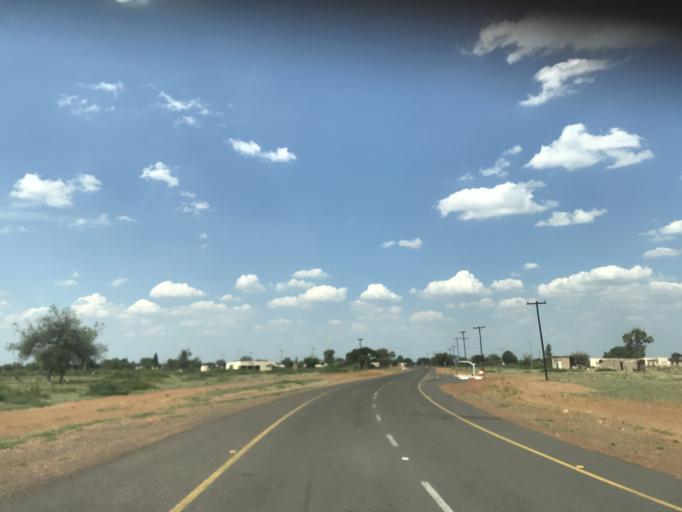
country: BW
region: South East
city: Janeng
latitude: -25.5632
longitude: 25.5894
